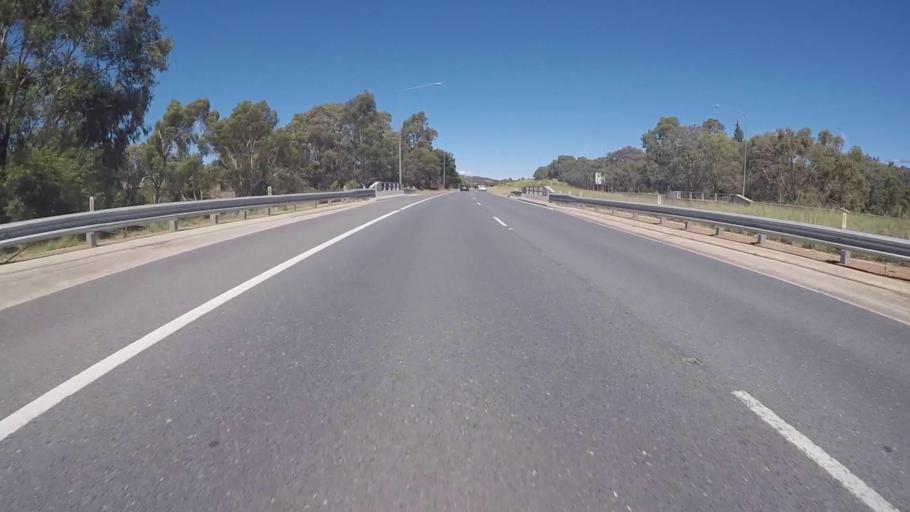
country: AU
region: Australian Capital Territory
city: Macarthur
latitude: -35.4169
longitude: 149.0754
